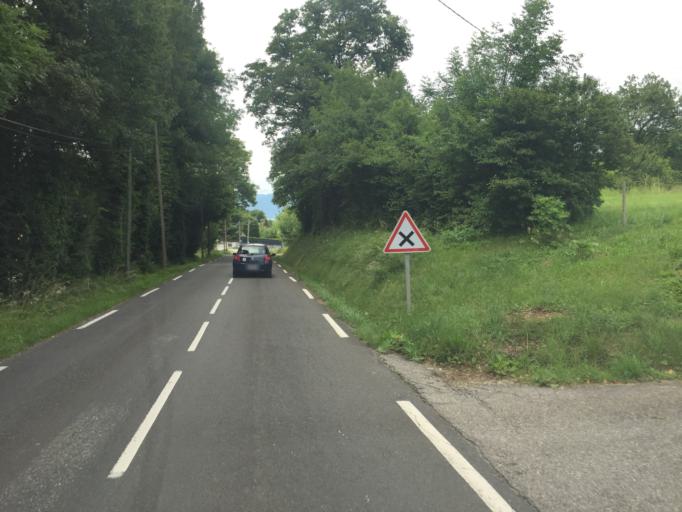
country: FR
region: Rhone-Alpes
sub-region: Departement de la Savoie
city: Jacob-Bellecombette
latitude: 45.5428
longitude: 5.9167
